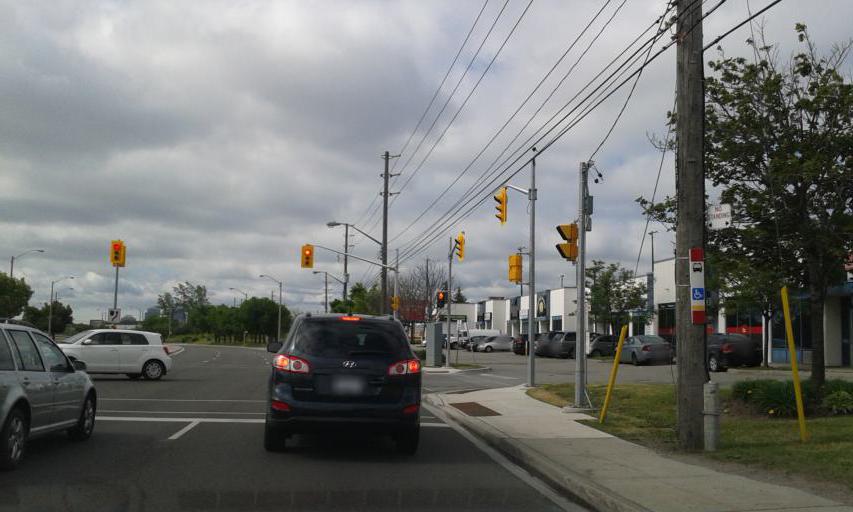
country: CA
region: Ontario
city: Scarborough
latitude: 43.8087
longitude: -79.2438
